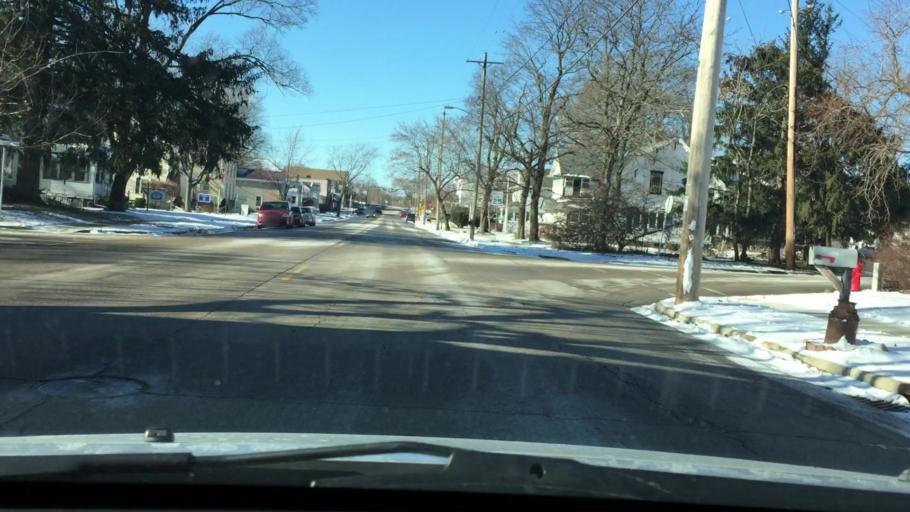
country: US
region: Wisconsin
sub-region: Waukesha County
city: Eagle
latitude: 42.8790
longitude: -88.4712
